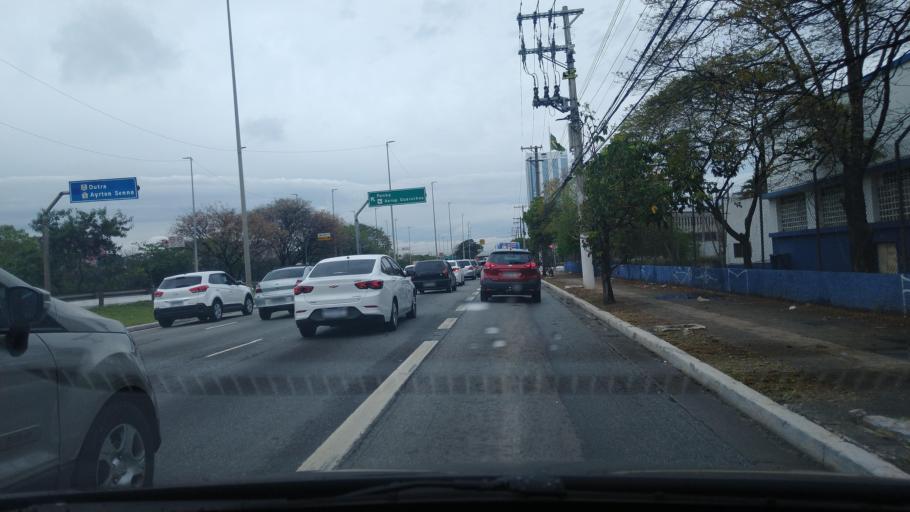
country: SA
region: Ar Riyad
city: Ad Dilam
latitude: 23.5154
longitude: 46.6725
